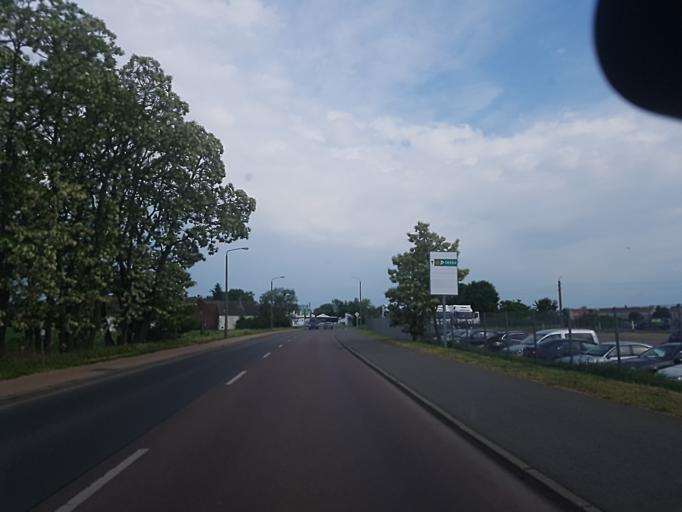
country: DE
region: Saxony-Anhalt
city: Wittenburg
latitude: 51.8732
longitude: 12.6163
